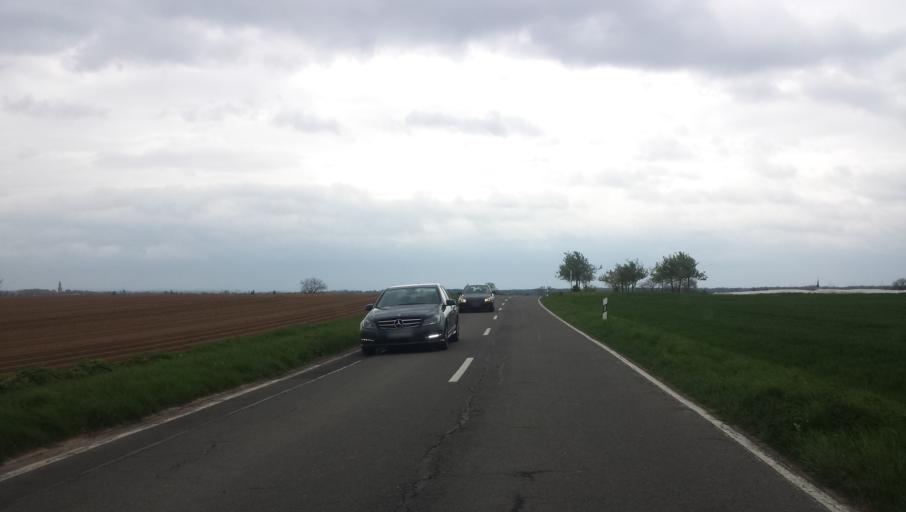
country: DE
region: Rheinland-Pfalz
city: Schwegenheim
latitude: 49.2601
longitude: 8.3238
